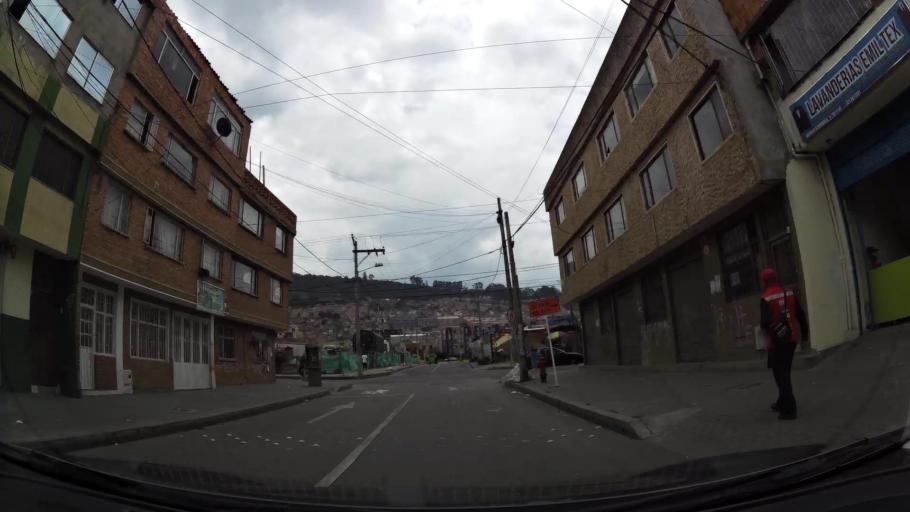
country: CO
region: Cundinamarca
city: La Calera
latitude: 4.7641
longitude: -74.0327
